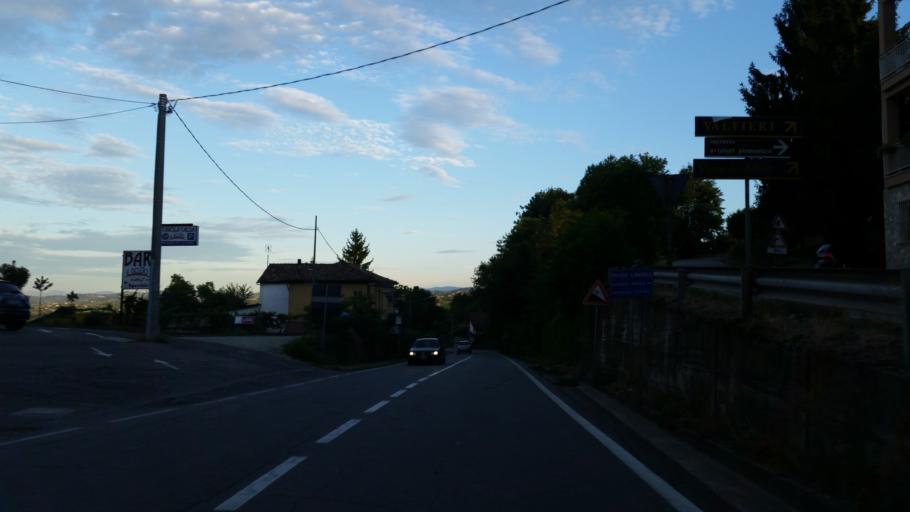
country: IT
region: Piedmont
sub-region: Provincia di Asti
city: Costigliole d'Asti
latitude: 44.7828
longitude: 8.1934
